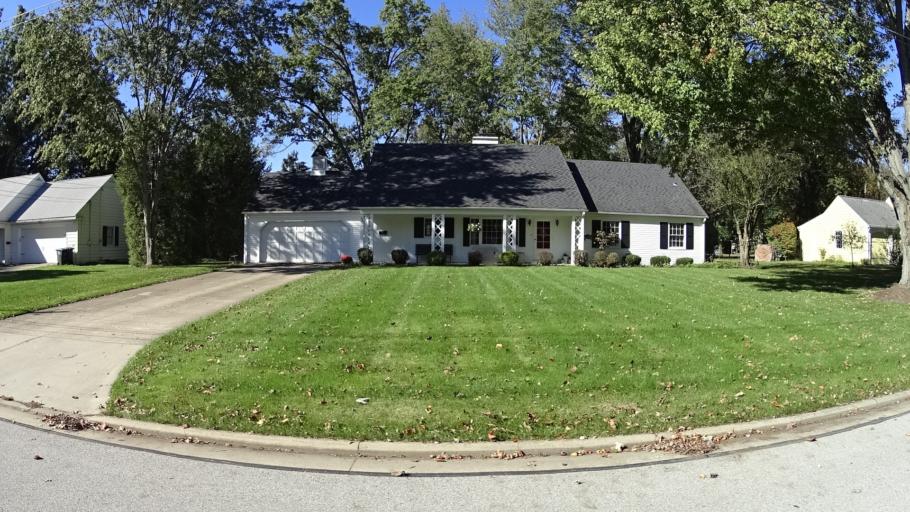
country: US
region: Ohio
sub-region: Lorain County
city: Oberlin
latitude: 41.2884
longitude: -82.2353
